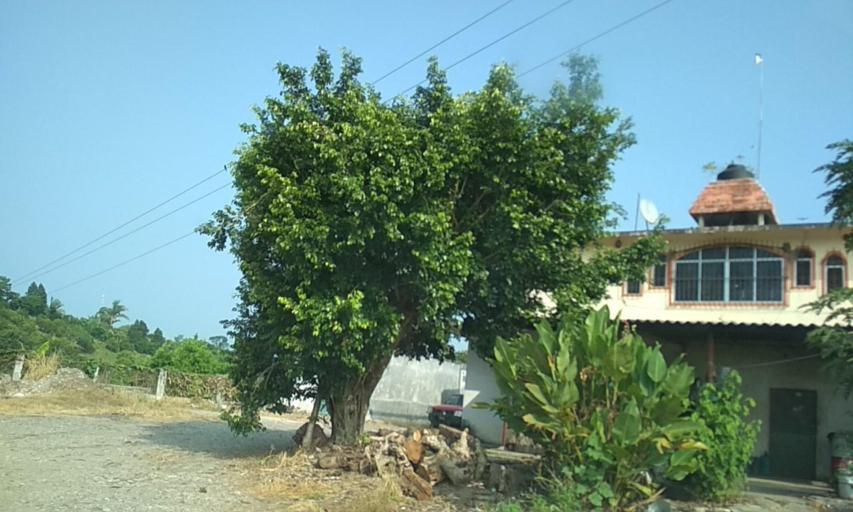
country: MX
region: Veracruz
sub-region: Misantla
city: La Defensa
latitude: 20.0511
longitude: -96.9819
